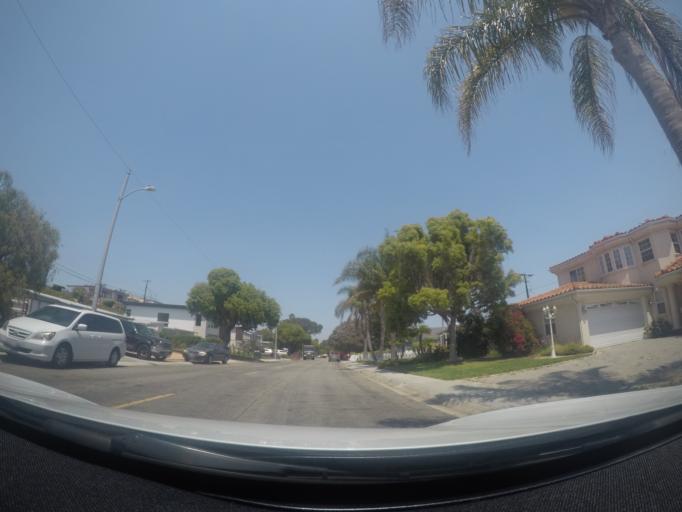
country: US
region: California
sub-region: Los Angeles County
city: Palos Verdes Estates
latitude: 33.8162
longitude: -118.3685
